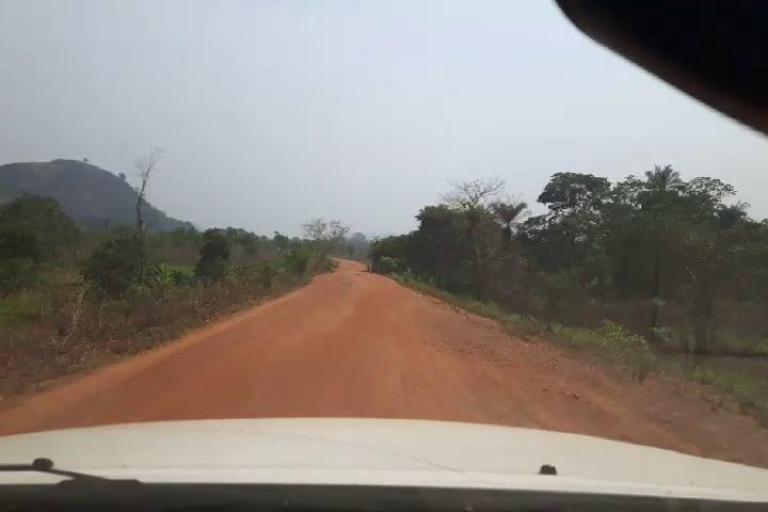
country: SL
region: Northern Province
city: Bumbuna
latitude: 8.9561
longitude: -11.8046
